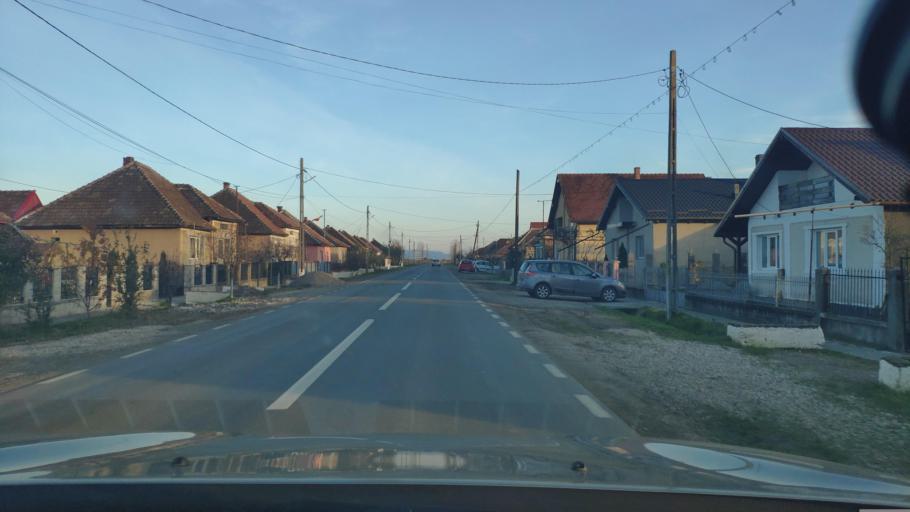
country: RO
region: Satu Mare
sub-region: Comuna Mediesu Aurit
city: Potau
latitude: 47.7740
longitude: 23.1031
